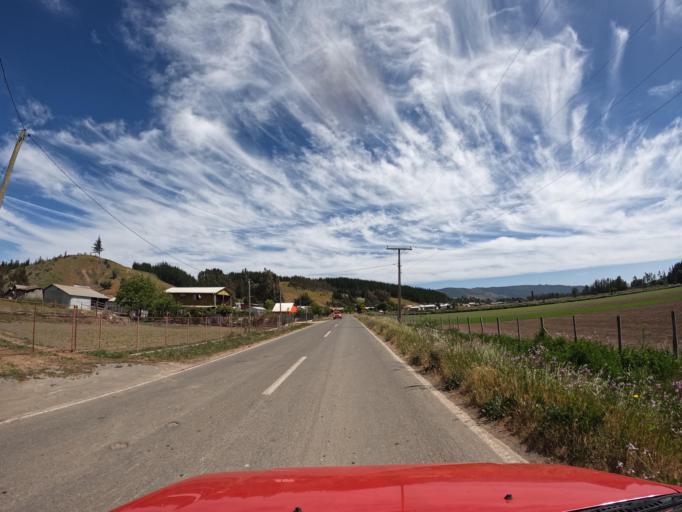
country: CL
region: Maule
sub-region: Provincia de Talca
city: Constitucion
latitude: -35.0203
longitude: -72.0398
